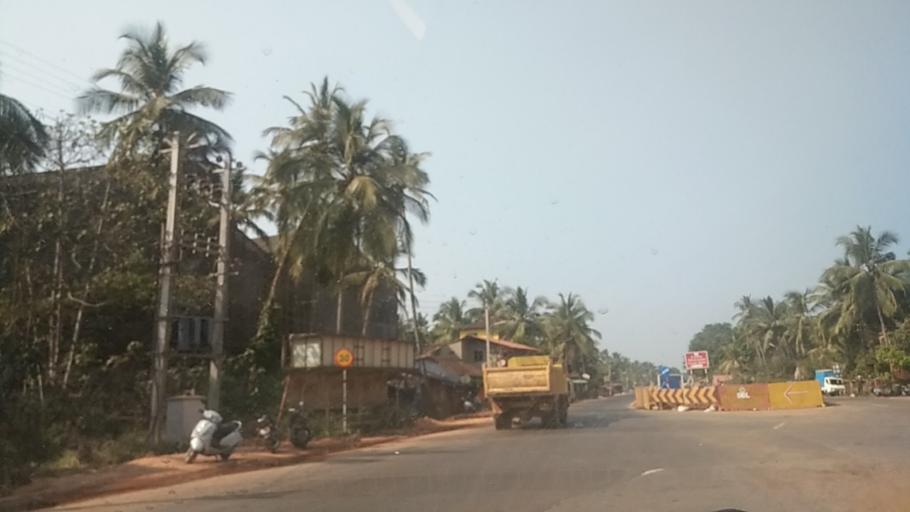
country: IN
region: Goa
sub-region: South Goa
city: Cortalim
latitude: 15.3979
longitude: 73.9105
